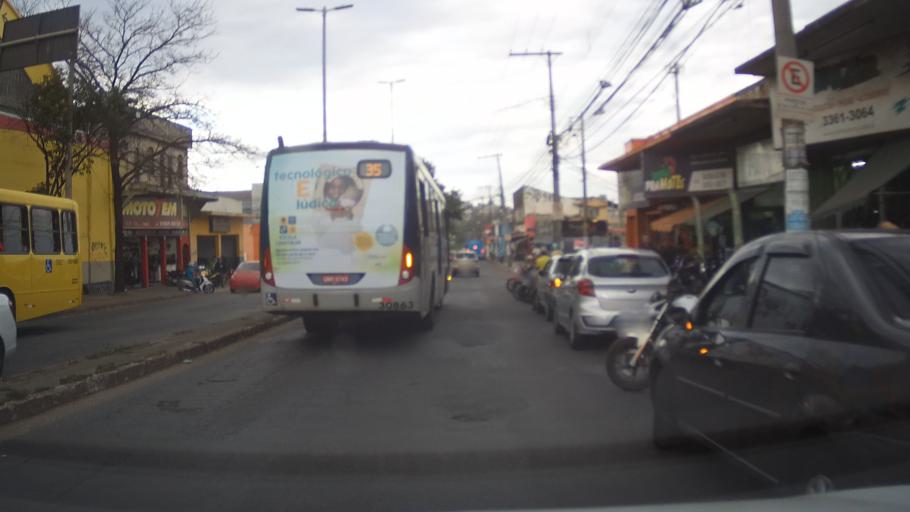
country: BR
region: Minas Gerais
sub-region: Contagem
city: Contagem
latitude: -19.9608
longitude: -44.0160
